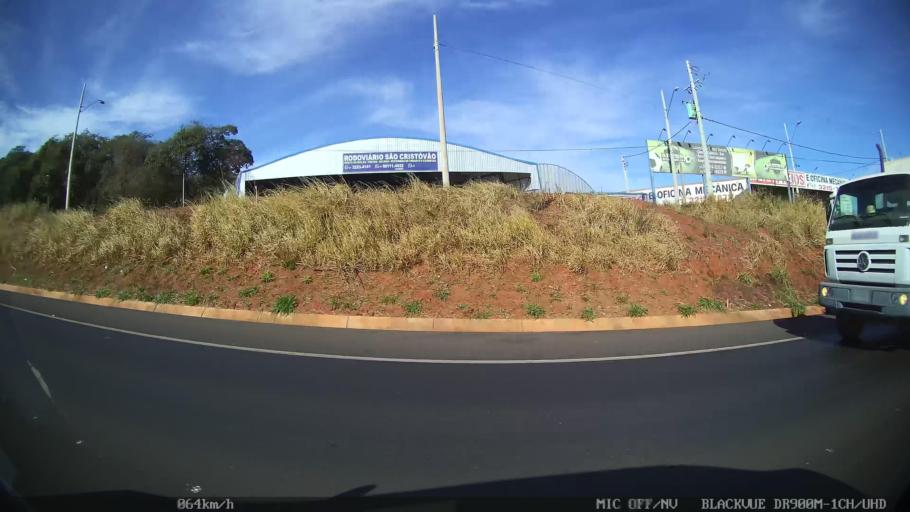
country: BR
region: Sao Paulo
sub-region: Sao Jose Do Rio Preto
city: Sao Jose do Rio Preto
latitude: -20.7707
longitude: -49.3500
